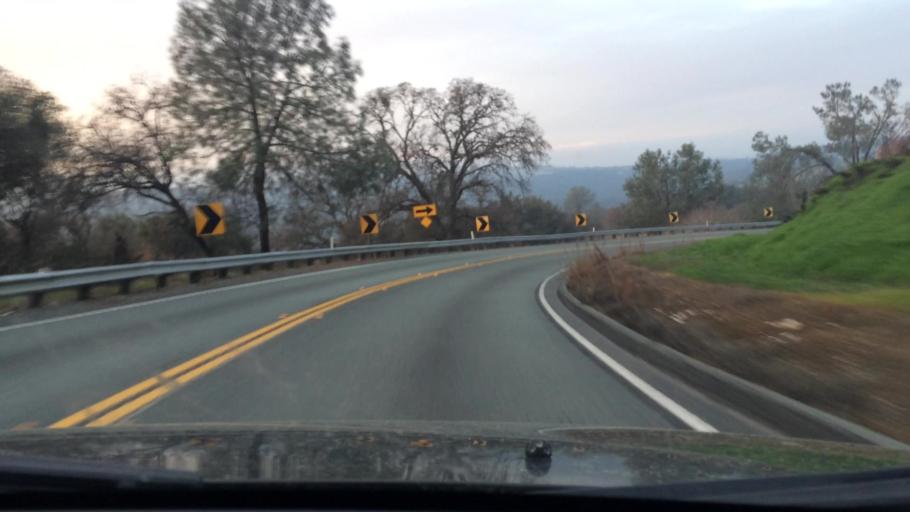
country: US
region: California
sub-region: Amador County
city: Jackson
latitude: 38.2996
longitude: -120.7335
